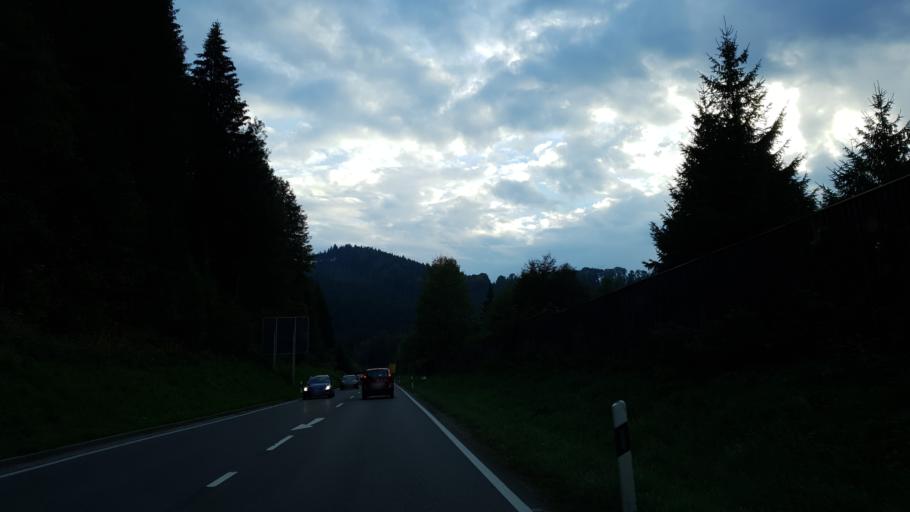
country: DE
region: Bavaria
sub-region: Swabia
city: Maierhofen
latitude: 47.6545
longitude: 10.0877
